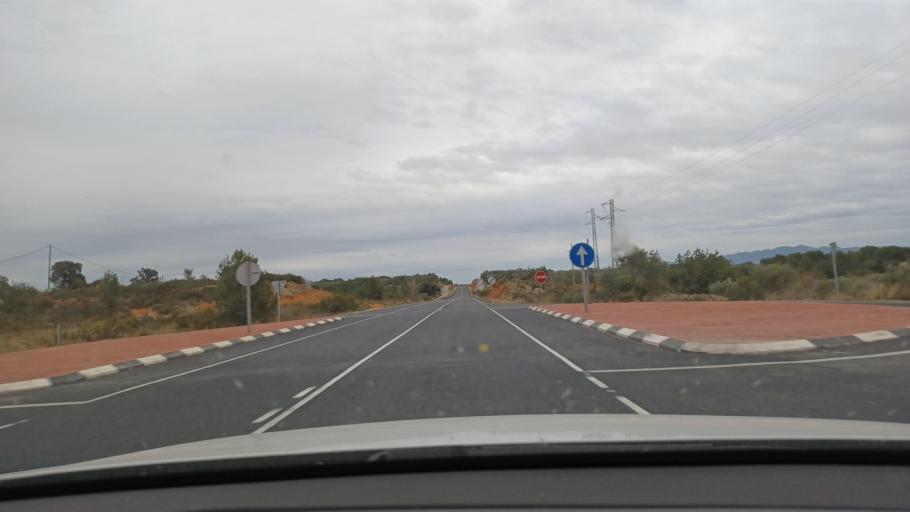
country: ES
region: Valencia
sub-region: Provincia de Castello
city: Traiguera
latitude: 40.5472
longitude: 0.3201
